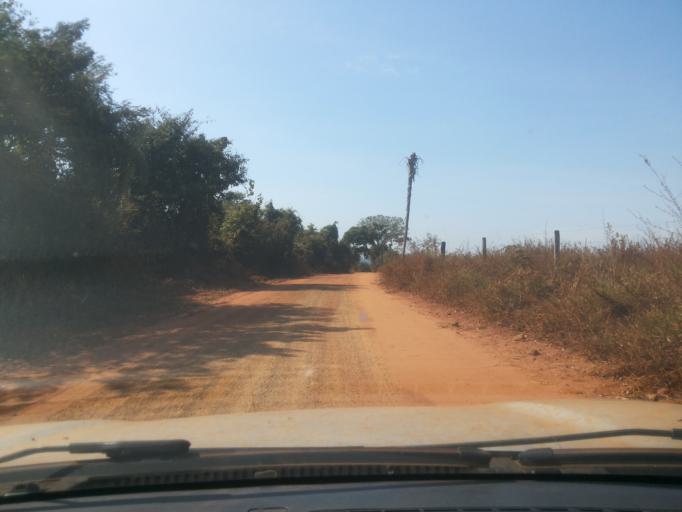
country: BR
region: Minas Gerais
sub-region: Ituiutaba
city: Ituiutaba
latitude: -19.0454
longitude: -49.3723
